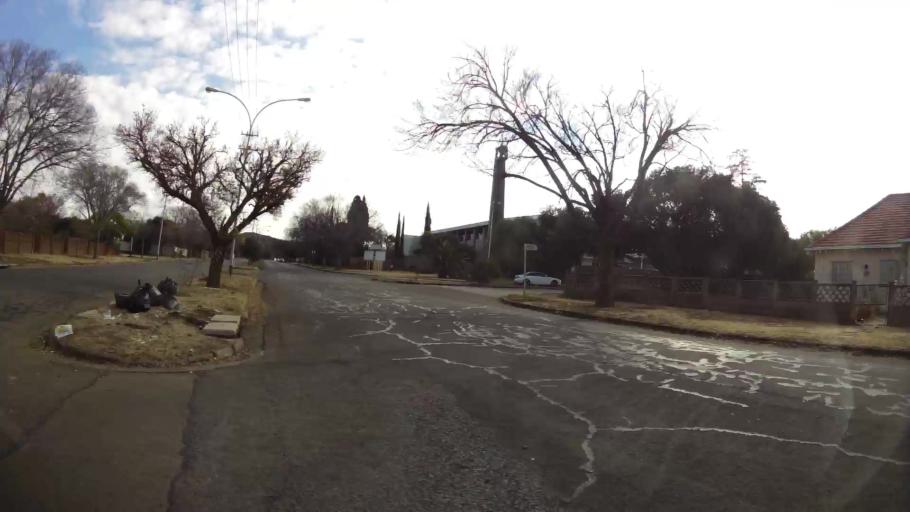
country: ZA
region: Orange Free State
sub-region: Mangaung Metropolitan Municipality
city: Bloemfontein
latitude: -29.0802
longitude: 26.2408
